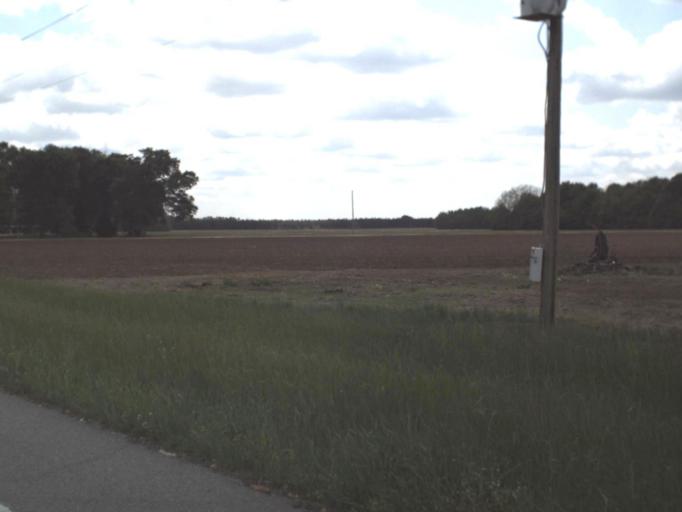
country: US
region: Alabama
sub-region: Escambia County
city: Atmore
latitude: 30.9691
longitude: -87.4868
